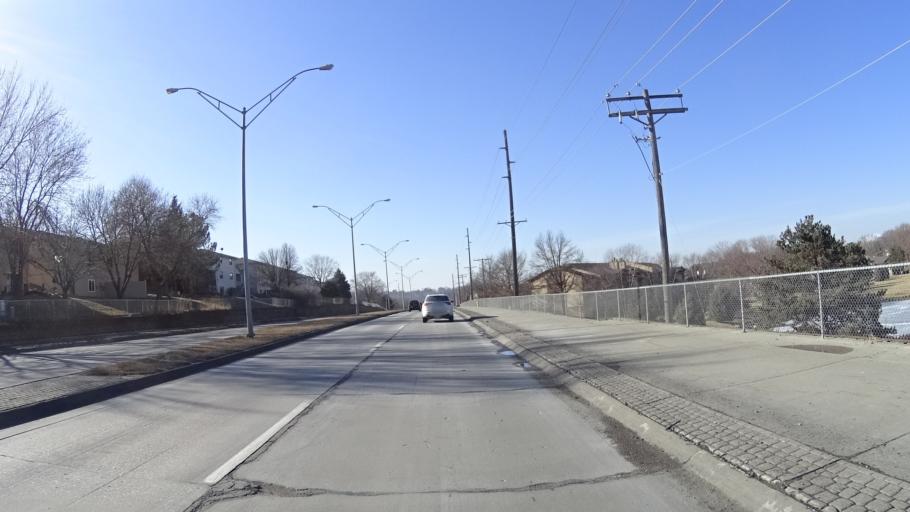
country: US
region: Nebraska
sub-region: Douglas County
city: Bennington
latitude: 41.3067
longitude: -96.0900
